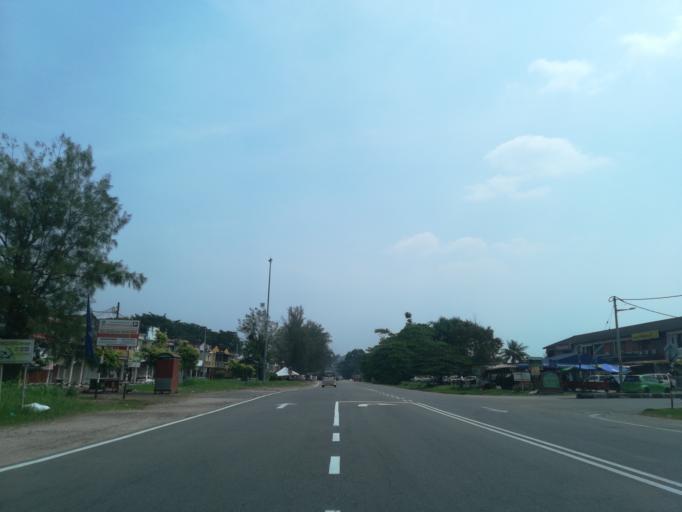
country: MY
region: Kedah
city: Kulim
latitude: 5.4233
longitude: 100.5372
